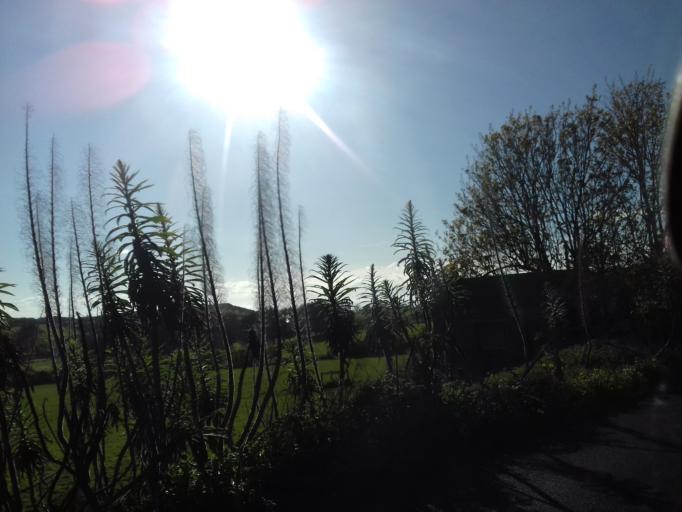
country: IE
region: Leinster
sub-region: Fingal County
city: Howth
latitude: 53.3682
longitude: -6.0814
